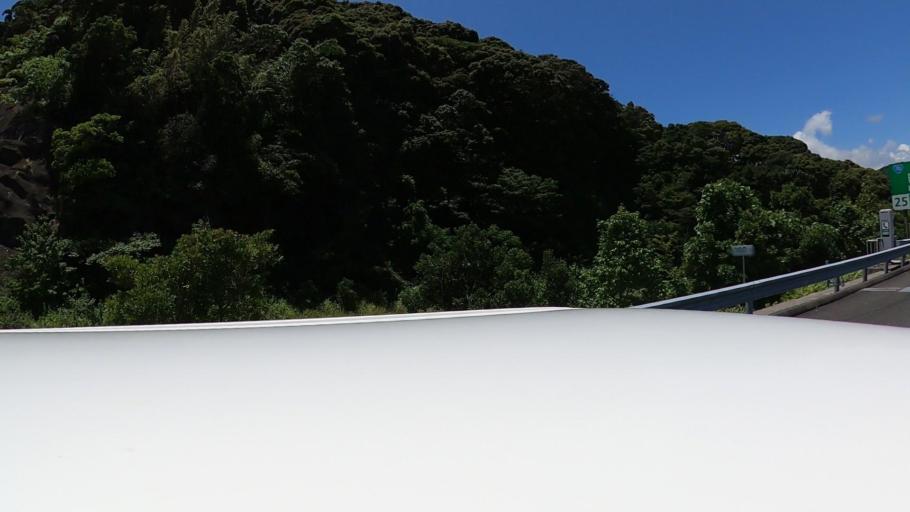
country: JP
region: Miyazaki
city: Nobeoka
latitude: 32.3956
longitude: 131.6201
